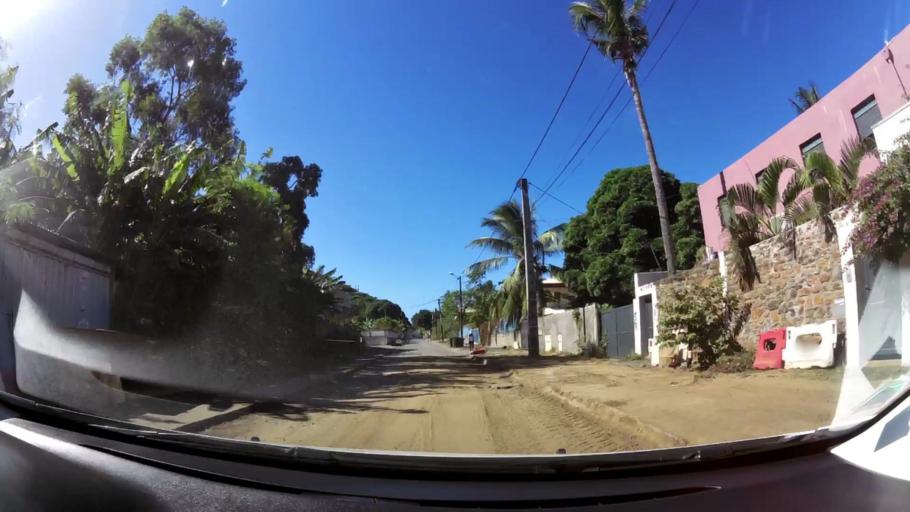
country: YT
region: Pamandzi
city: Pamandzi
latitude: -12.7850
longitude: 45.2742
